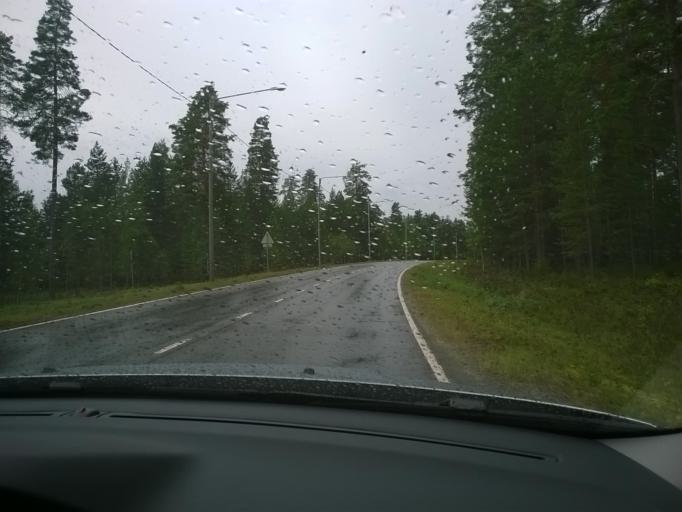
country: FI
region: Kainuu
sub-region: Kehys-Kainuu
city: Kuhmo
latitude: 64.1215
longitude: 29.5403
